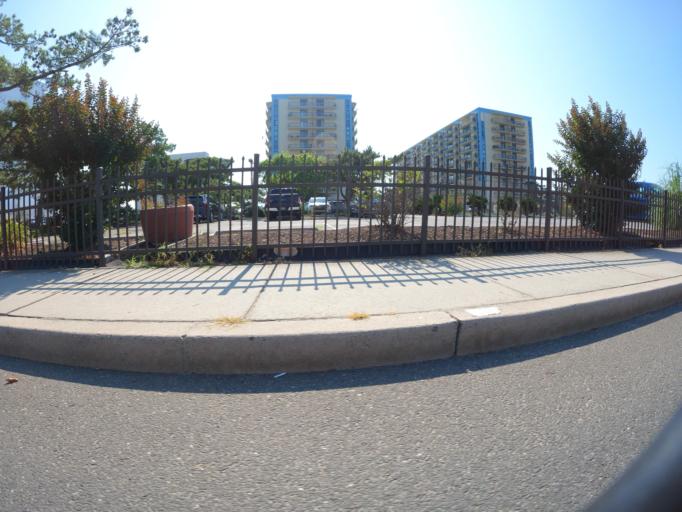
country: US
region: Delaware
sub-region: Sussex County
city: Bethany Beach
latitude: 38.4373
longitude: -75.0536
